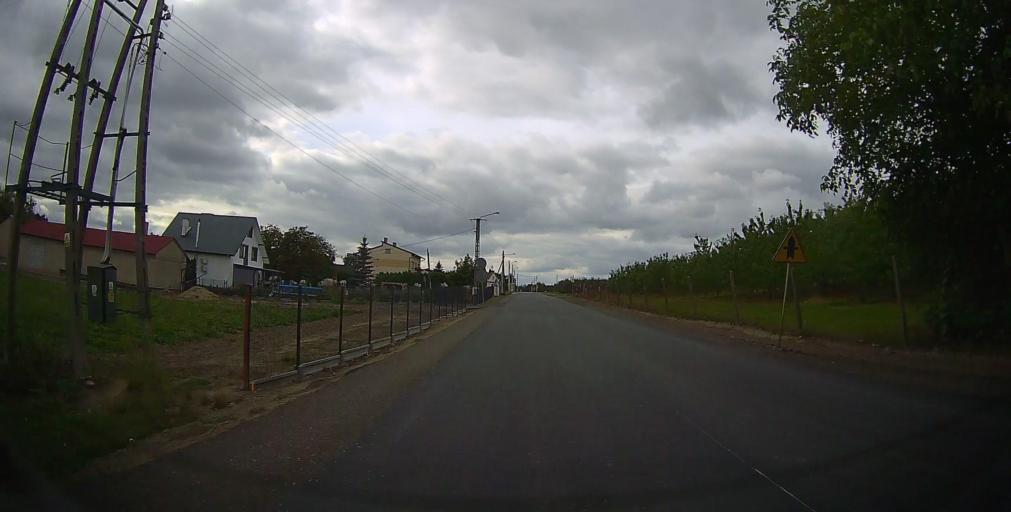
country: PL
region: Masovian Voivodeship
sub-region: Powiat grojecki
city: Belsk Duzy
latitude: 51.8088
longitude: 20.8436
